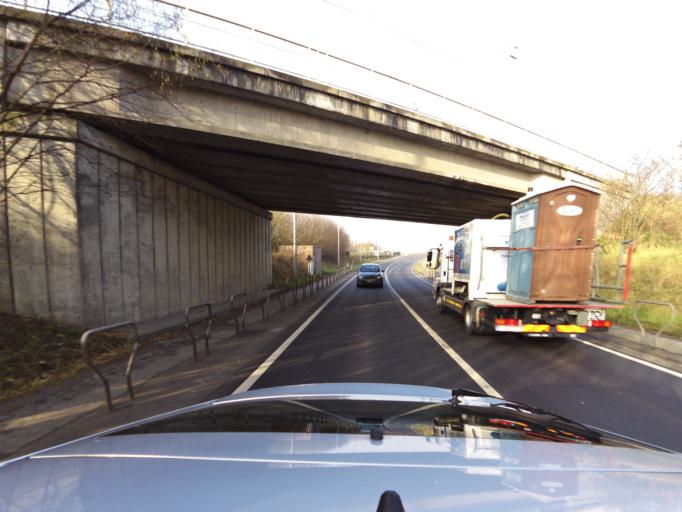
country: BE
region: Flanders
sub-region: Provincie West-Vlaanderen
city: Lichtervelde
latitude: 51.0173
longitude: 3.1365
